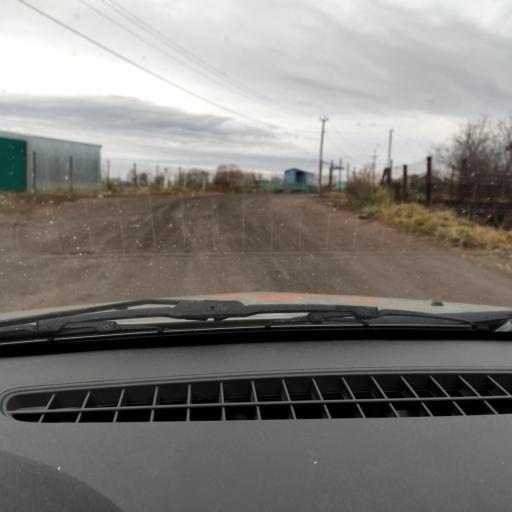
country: RU
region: Bashkortostan
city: Mikhaylovka
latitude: 54.8371
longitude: 55.9446
